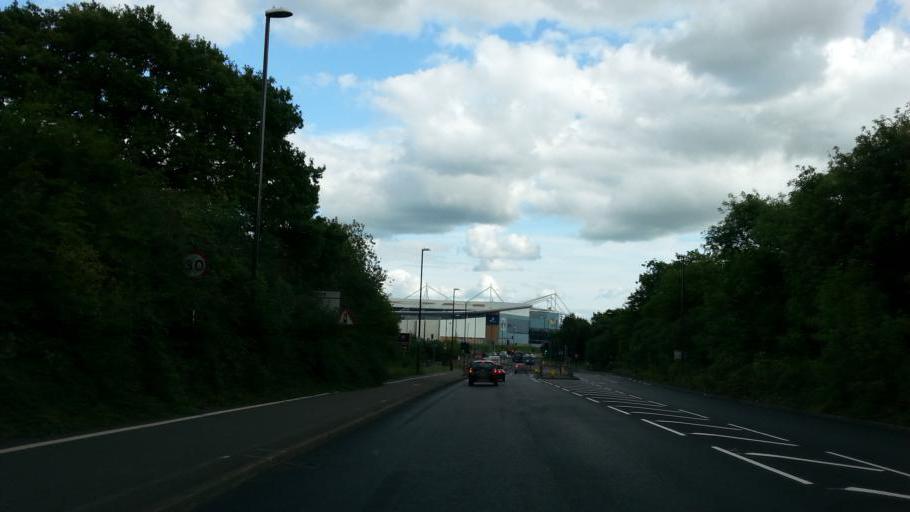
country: GB
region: England
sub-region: Warwickshire
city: Exhall
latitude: 52.4497
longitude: -1.5027
